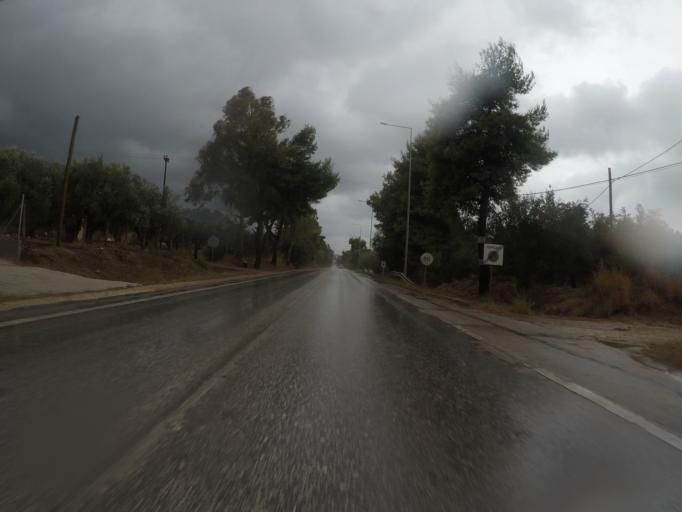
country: GR
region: Peloponnese
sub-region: Nomos Messinias
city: Kyparissia
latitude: 37.2593
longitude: 21.6835
